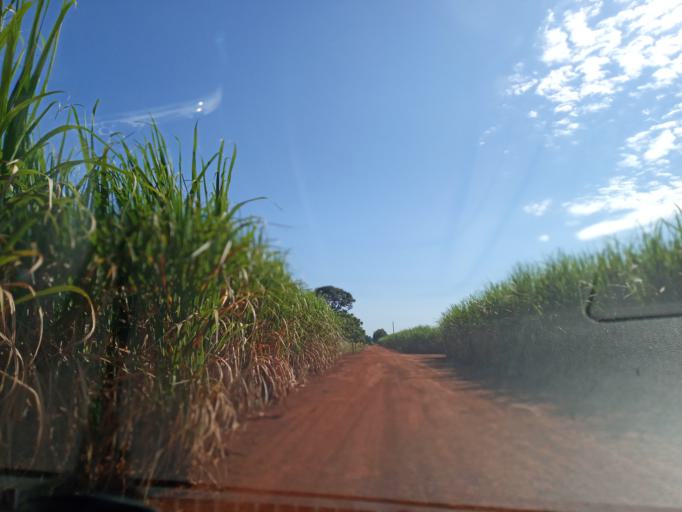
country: BR
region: Goias
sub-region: Itumbiara
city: Itumbiara
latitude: -18.4642
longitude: -49.1219
